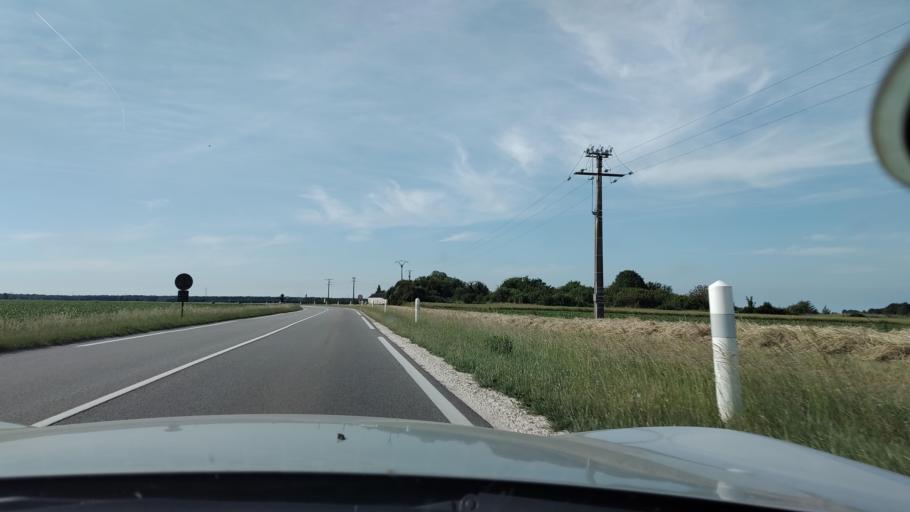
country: FR
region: Ile-de-France
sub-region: Departement de Seine-et-Marne
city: Jouy-le-Chatel
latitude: 48.6642
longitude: 3.1386
